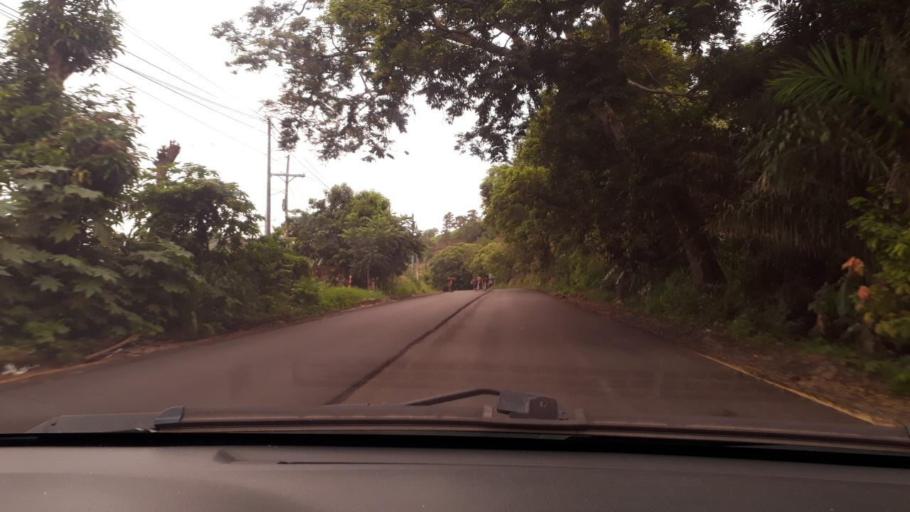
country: GT
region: Chiquimula
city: Concepcion Las Minas
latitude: 14.5424
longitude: -89.4625
